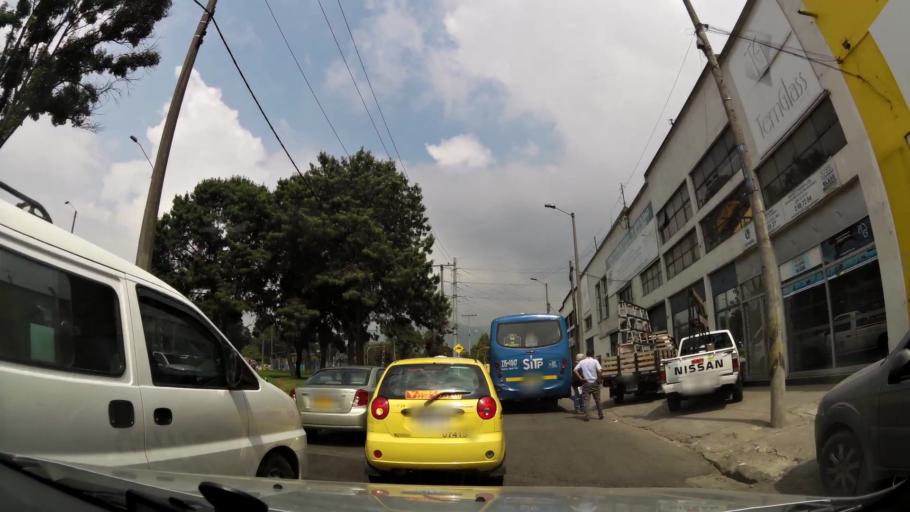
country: CO
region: Bogota D.C.
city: Bogota
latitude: 4.6253
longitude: -74.0919
